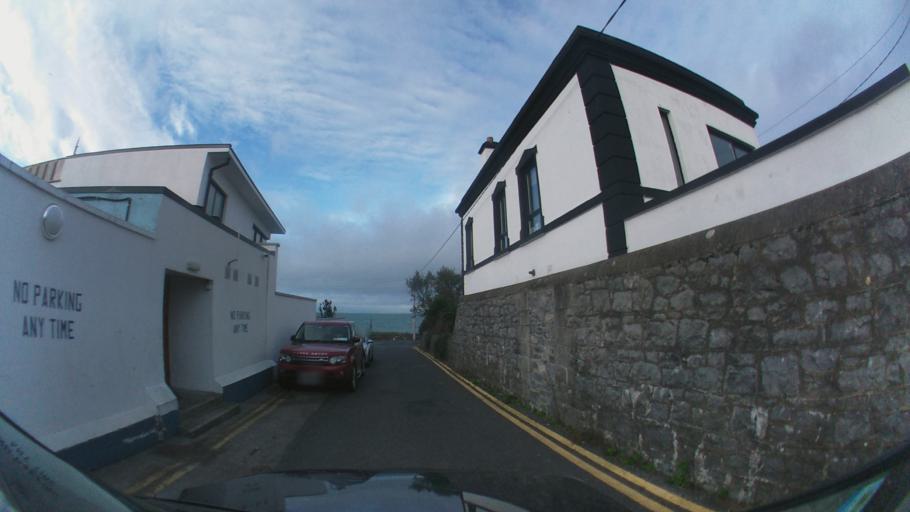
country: IE
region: Leinster
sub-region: Fingal County
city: Skerries
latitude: 53.5851
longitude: -6.1045
